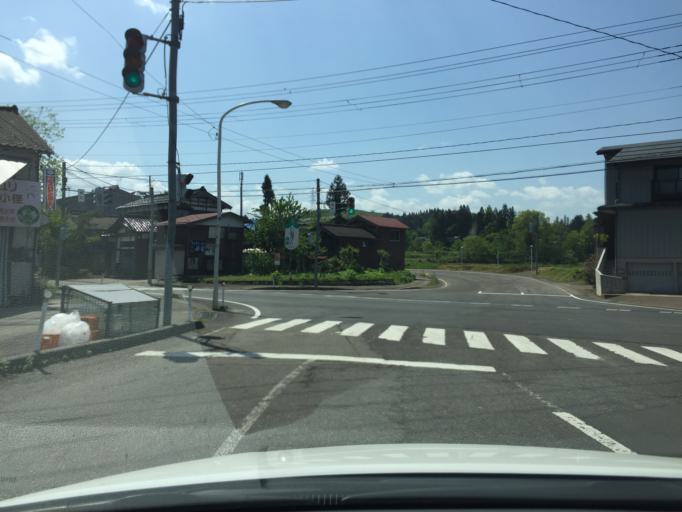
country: JP
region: Niigata
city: Tochio-honcho
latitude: 37.5452
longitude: 139.0916
